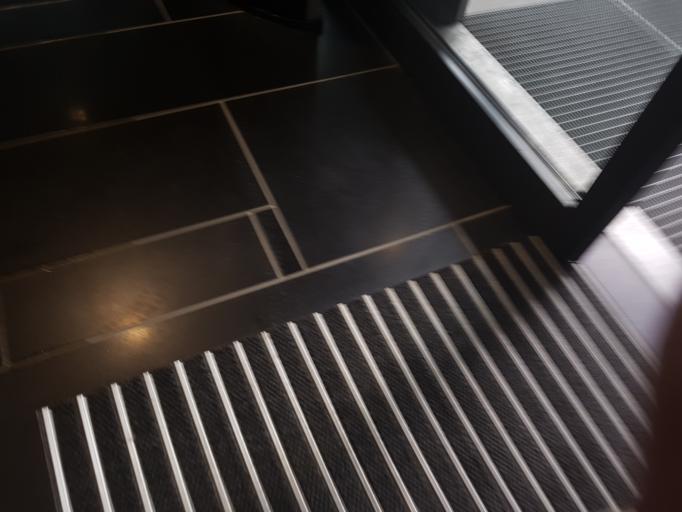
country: NO
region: Buskerud
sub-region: Drammen
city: Drammen
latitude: 59.7429
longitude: 10.1932
